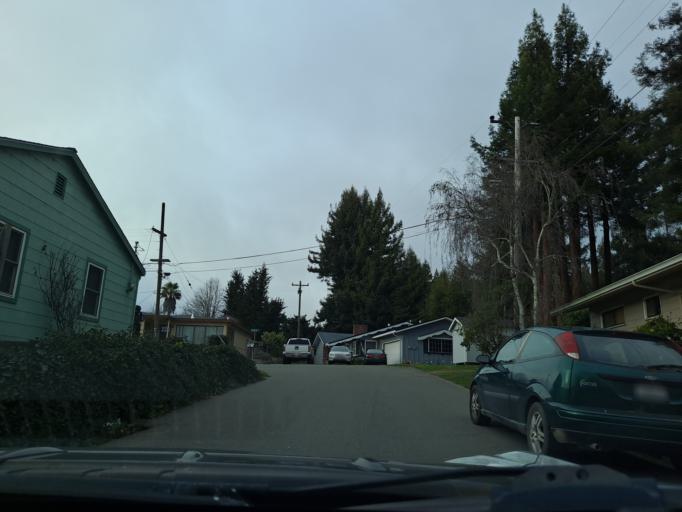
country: US
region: California
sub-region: Humboldt County
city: Fortuna
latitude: 40.6028
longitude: -124.1544
